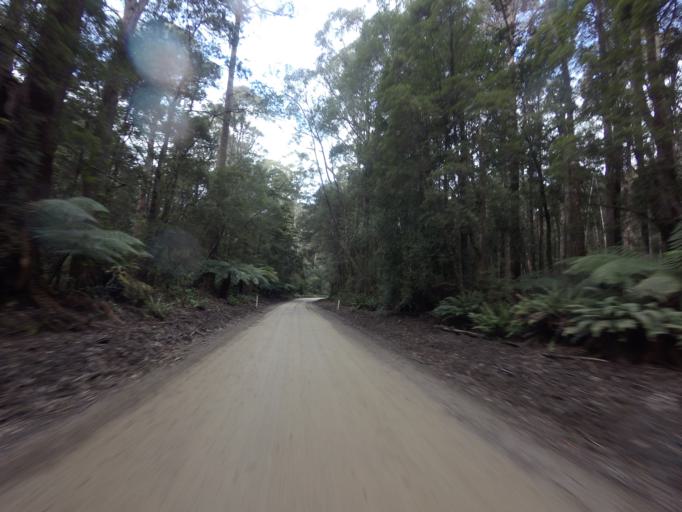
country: AU
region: Tasmania
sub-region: Huon Valley
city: Geeveston
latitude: -43.3873
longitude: 146.8489
